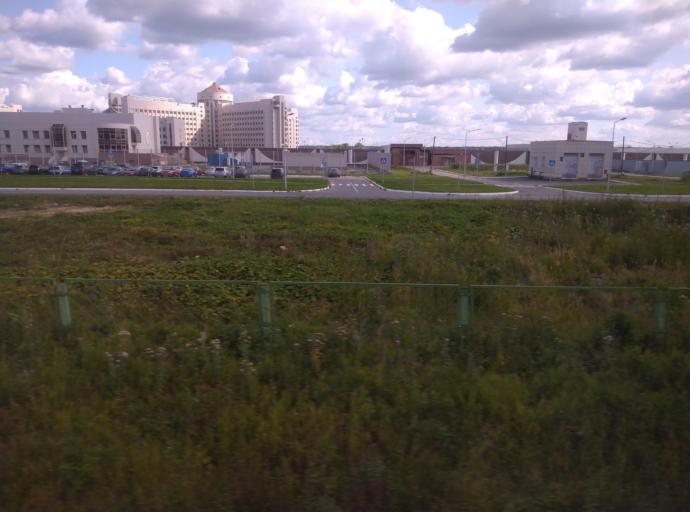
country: RU
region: St.-Petersburg
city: Kolpino
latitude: 59.7364
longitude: 30.6306
